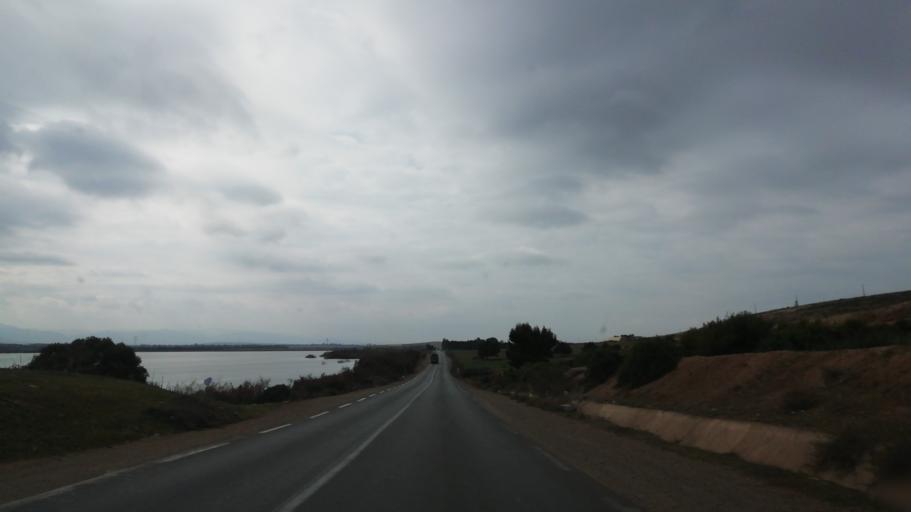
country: DZ
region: Oran
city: Sidi ech Chahmi
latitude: 35.6065
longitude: -0.4328
